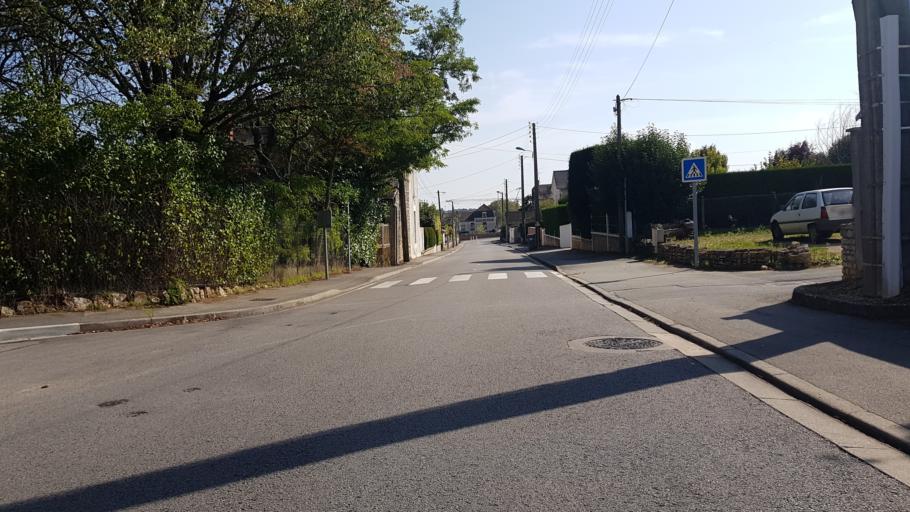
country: FR
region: Poitou-Charentes
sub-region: Departement de la Vienne
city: Chasseneuil-du-Poitou
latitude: 46.6524
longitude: 0.3706
